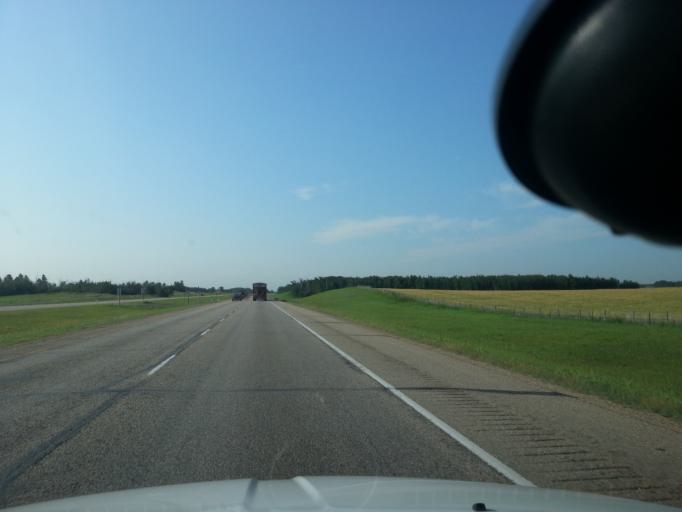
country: CA
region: Alberta
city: Millet
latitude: 52.9486
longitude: -113.6453
